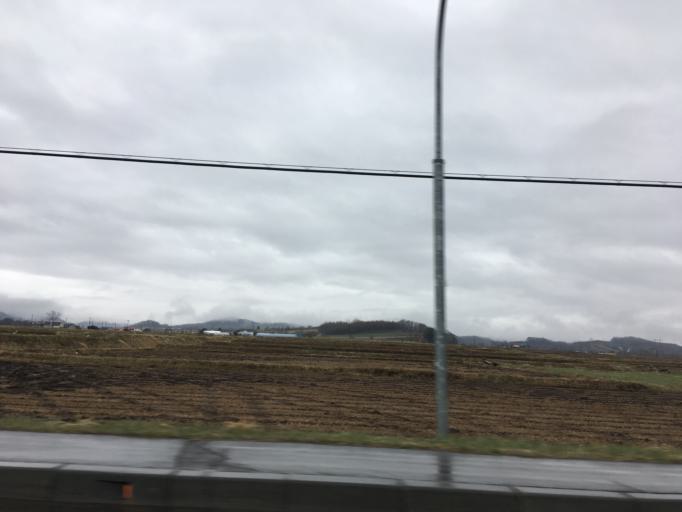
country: JP
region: Hokkaido
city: Nayoro
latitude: 44.1193
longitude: 142.4817
